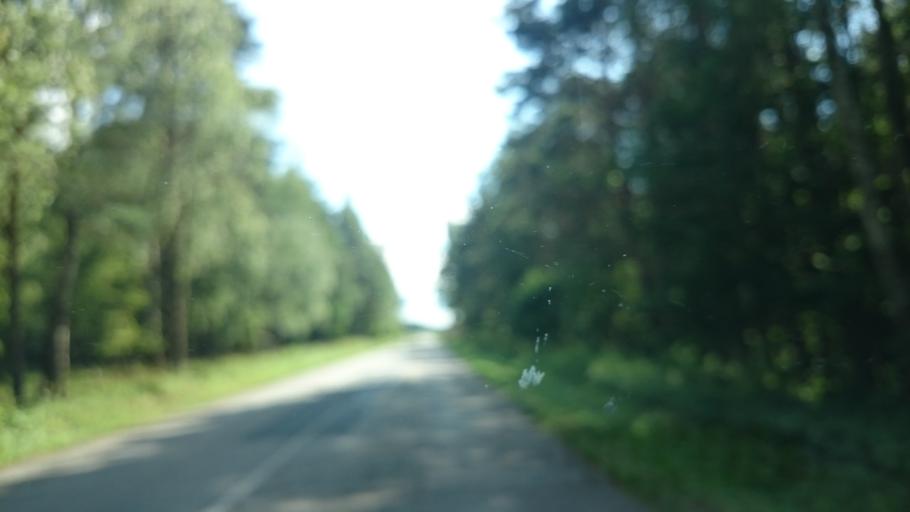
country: EE
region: Saare
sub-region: Orissaare vald
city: Orissaare
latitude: 58.5797
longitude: 22.7650
